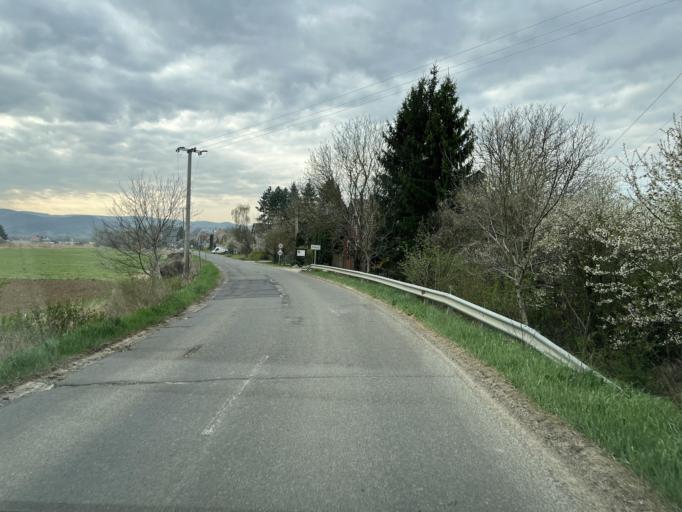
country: HU
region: Pest
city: Kosd
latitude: 47.8107
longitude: 19.2437
